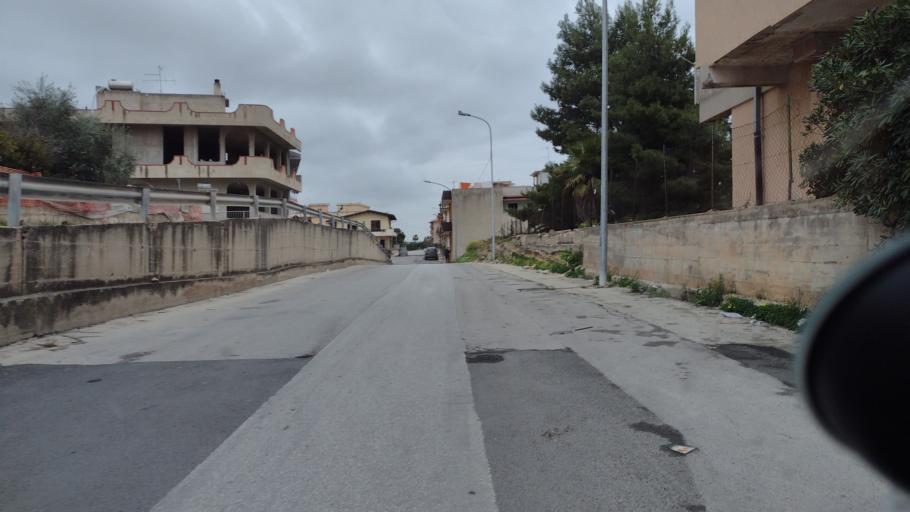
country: IT
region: Sicily
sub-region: Provincia di Siracusa
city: Avola
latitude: 36.9149
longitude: 15.1386
